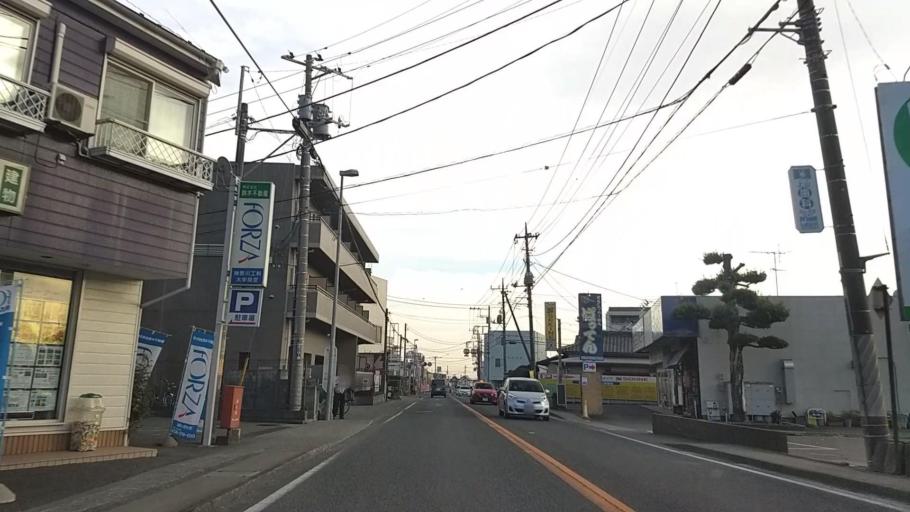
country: JP
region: Kanagawa
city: Atsugi
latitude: 35.4732
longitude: 139.3462
